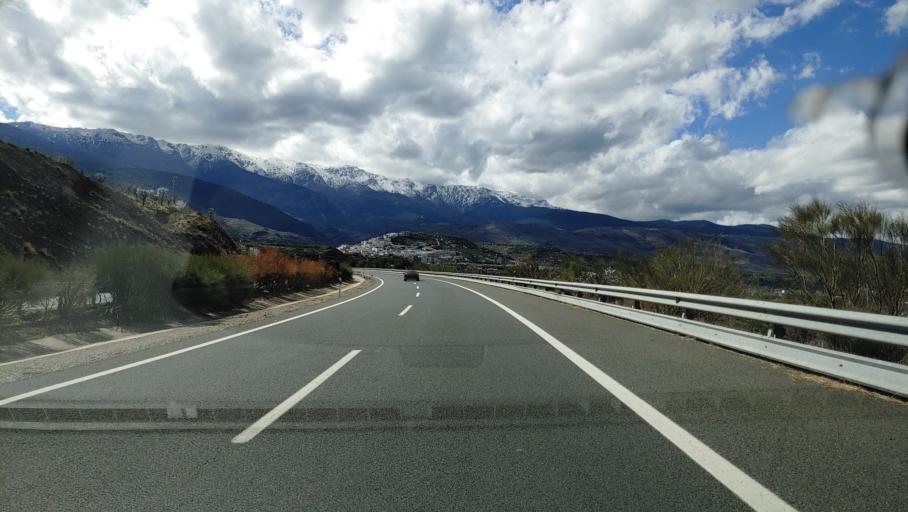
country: ES
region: Andalusia
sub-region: Provincia de Almeria
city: Abla
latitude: 37.1516
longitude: -2.7654
